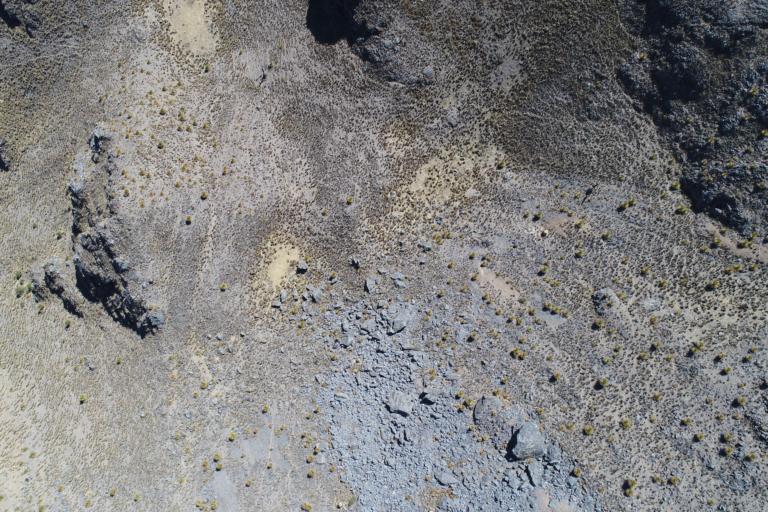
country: BO
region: La Paz
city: Viloco
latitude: -16.8101
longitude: -67.5456
